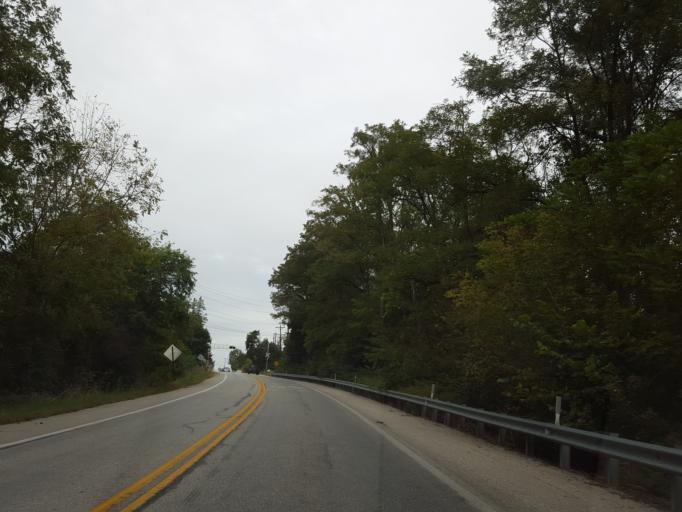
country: US
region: Pennsylvania
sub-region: York County
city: Shiloh
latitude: 39.9228
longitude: -76.7994
